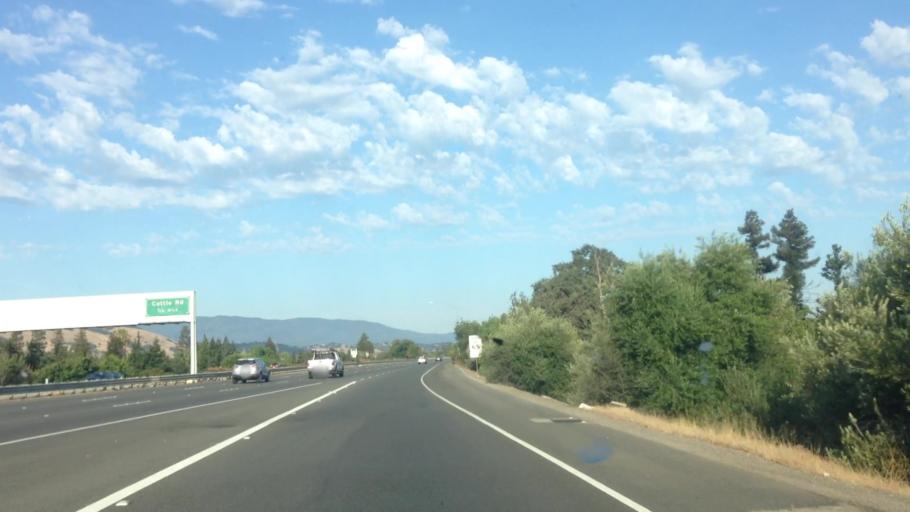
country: US
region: California
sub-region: Santa Clara County
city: Seven Trees
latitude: 37.2402
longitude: -121.7839
